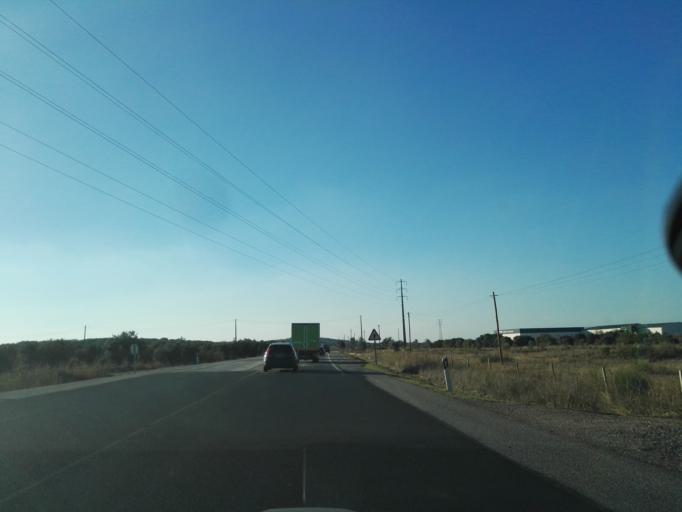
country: PT
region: Evora
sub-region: Borba
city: Borba
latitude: 38.8214
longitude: -7.4966
